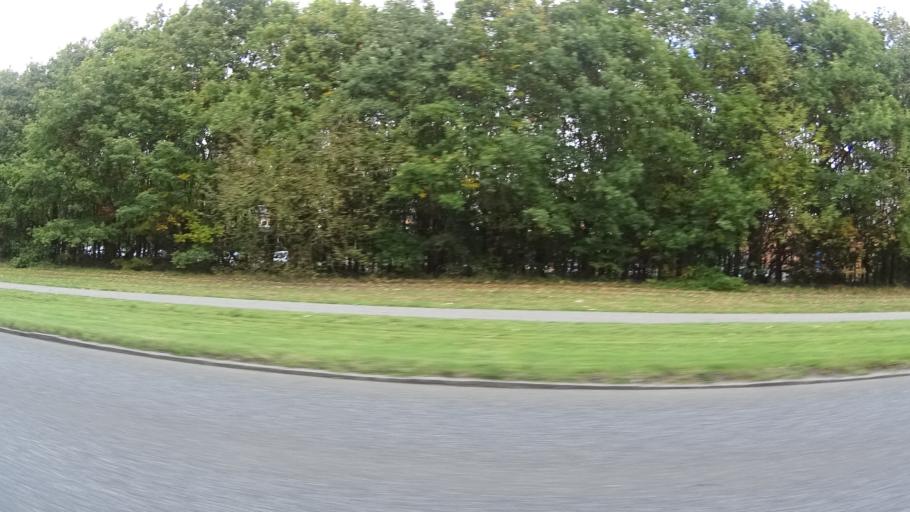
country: DK
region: South Denmark
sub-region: Vejle Kommune
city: Vejle
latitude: 55.6676
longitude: 9.5421
